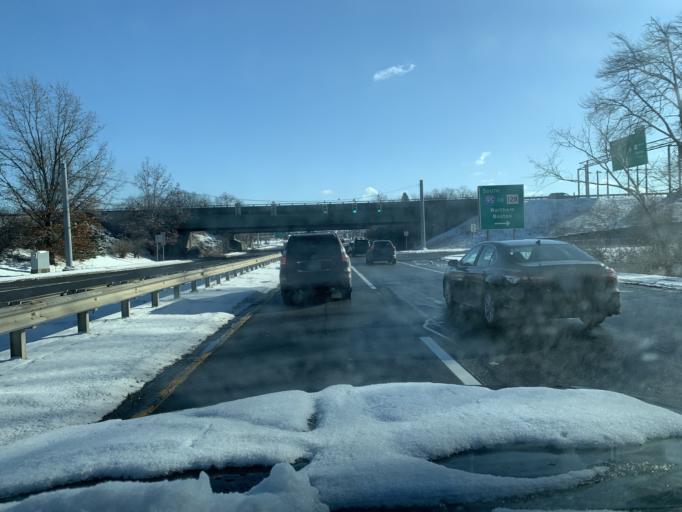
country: US
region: Massachusetts
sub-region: Essex County
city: Danvers
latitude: 42.5600
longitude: -70.9755
